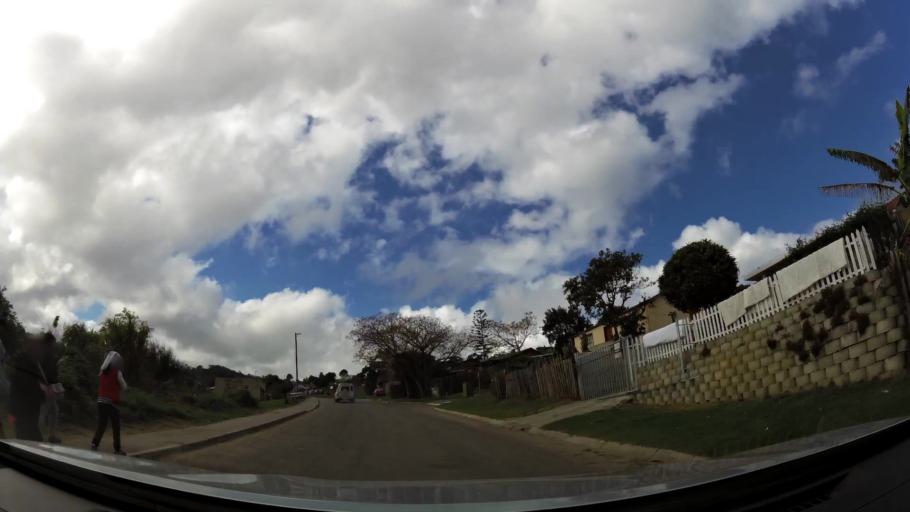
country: ZA
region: Western Cape
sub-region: Eden District Municipality
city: Knysna
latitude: -34.0508
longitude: 23.0942
